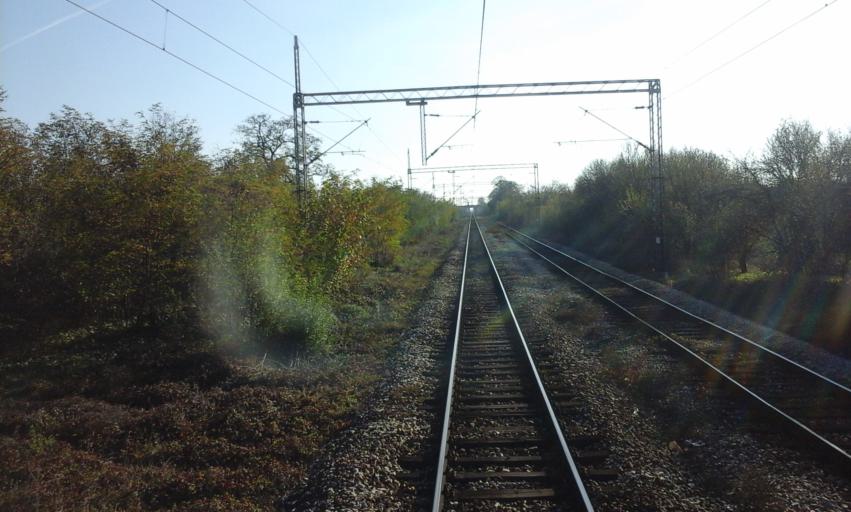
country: RS
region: Autonomna Pokrajina Vojvodina
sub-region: Severnobacki Okrug
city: Mali Igos
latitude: 45.7492
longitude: 19.6488
